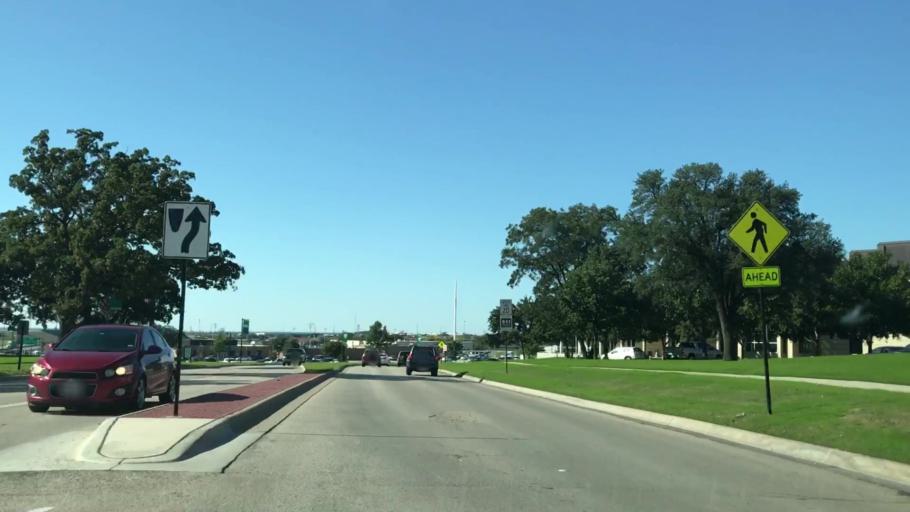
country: US
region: Texas
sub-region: Denton County
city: Denton
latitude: 33.2066
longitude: -97.1537
